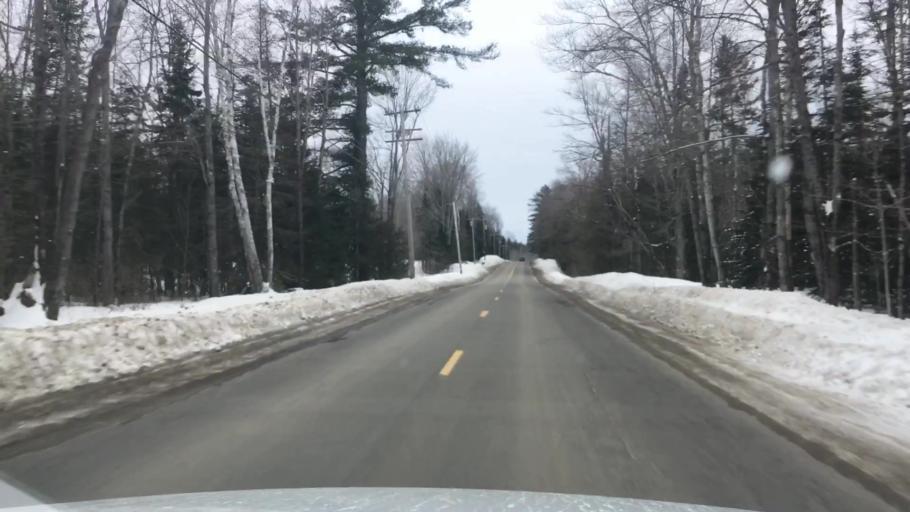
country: US
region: Maine
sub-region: Penobscot County
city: Charleston
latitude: 45.0501
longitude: -69.0298
